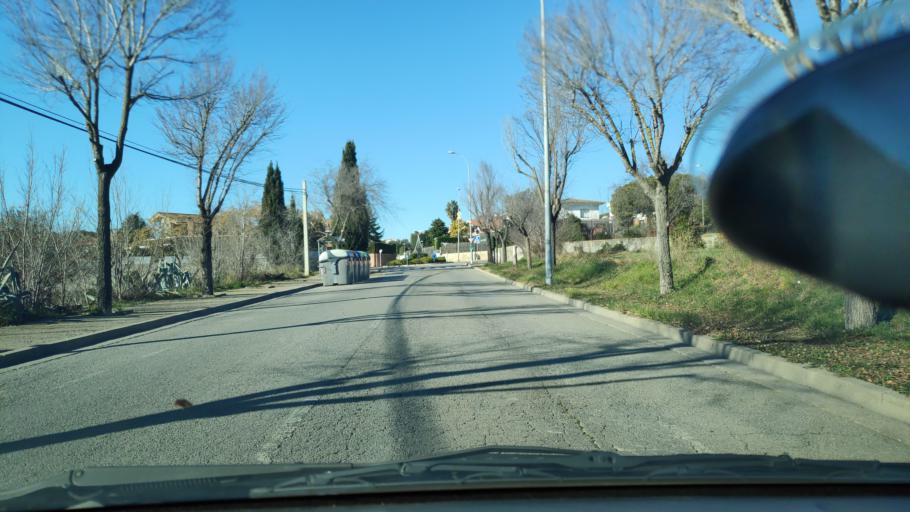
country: ES
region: Catalonia
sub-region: Provincia de Barcelona
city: Sant Quirze del Valles
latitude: 41.5381
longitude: 2.0674
